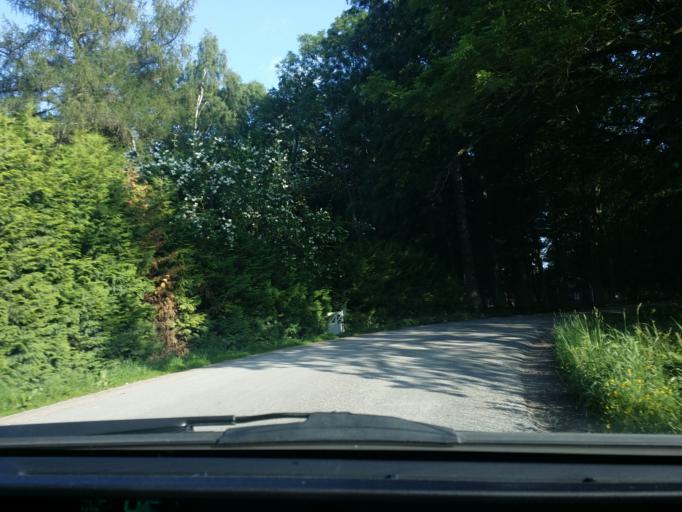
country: SE
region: Vaestmanland
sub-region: Vasteras
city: Vasteras
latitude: 59.5597
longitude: 16.6618
